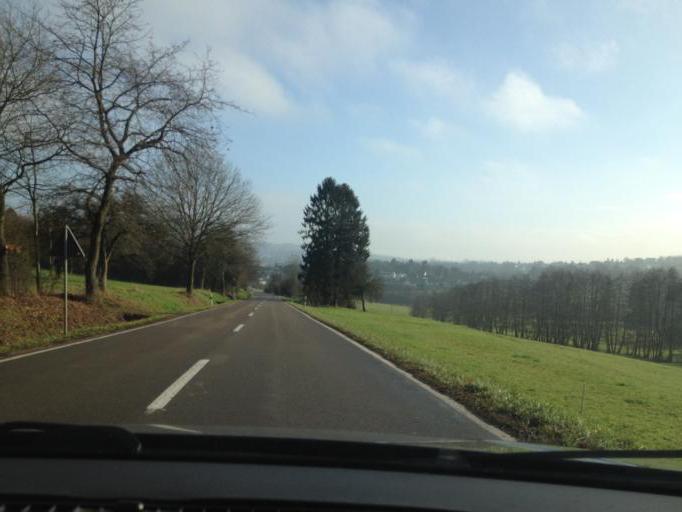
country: DE
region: Saarland
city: Mainzweiler
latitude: 49.4087
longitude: 7.1368
